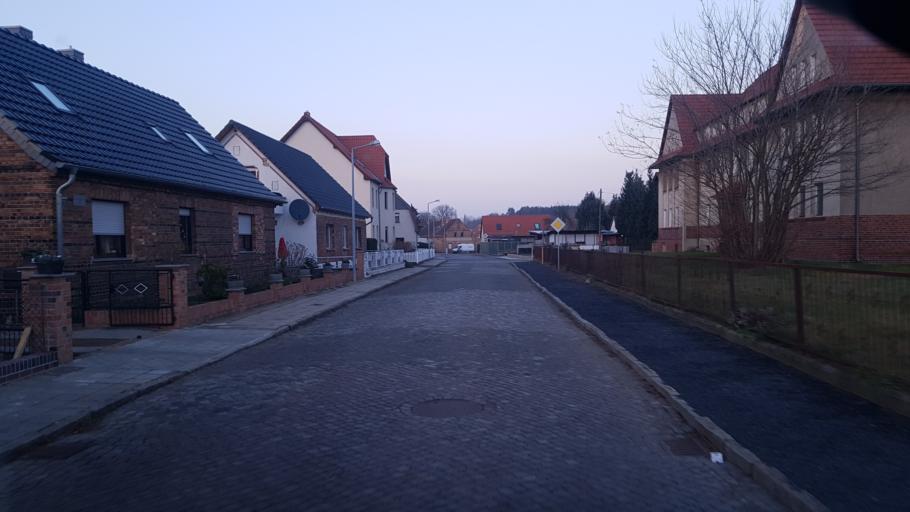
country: DE
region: Brandenburg
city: Lauchhammer
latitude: 51.5099
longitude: 13.7563
